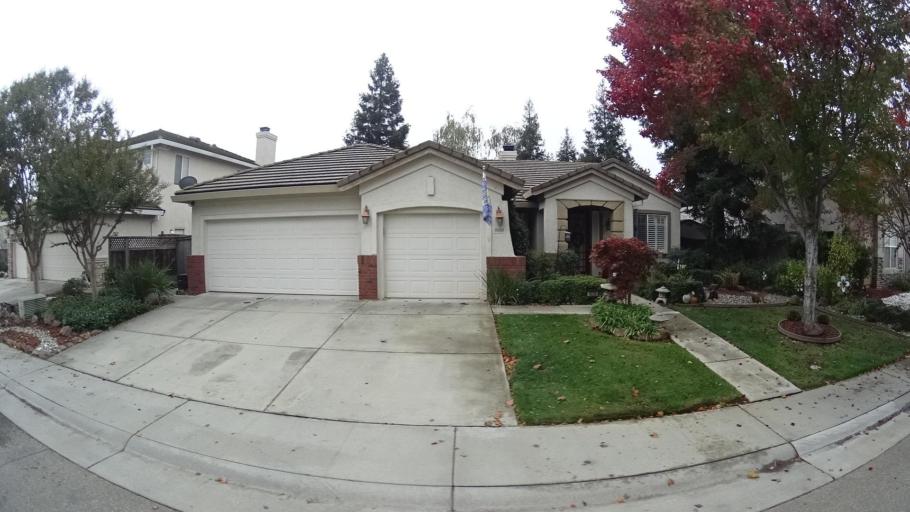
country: US
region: California
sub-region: Sacramento County
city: Elk Grove
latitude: 38.4121
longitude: -121.3449
